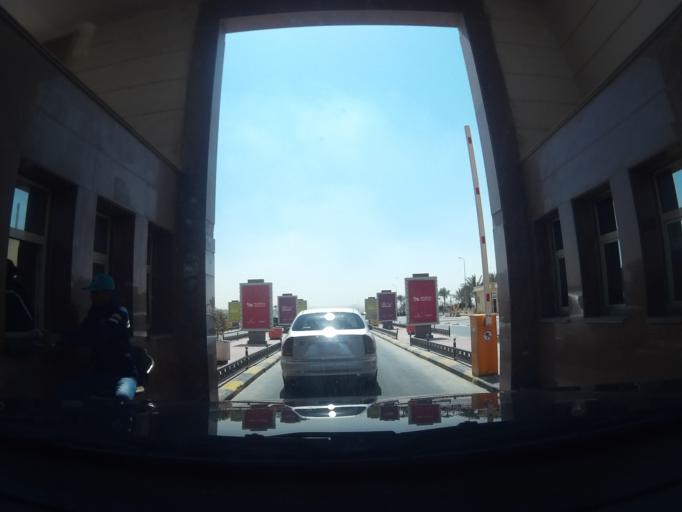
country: EG
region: As Suways
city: Ain Sukhna
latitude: 29.7667
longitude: 31.9433
